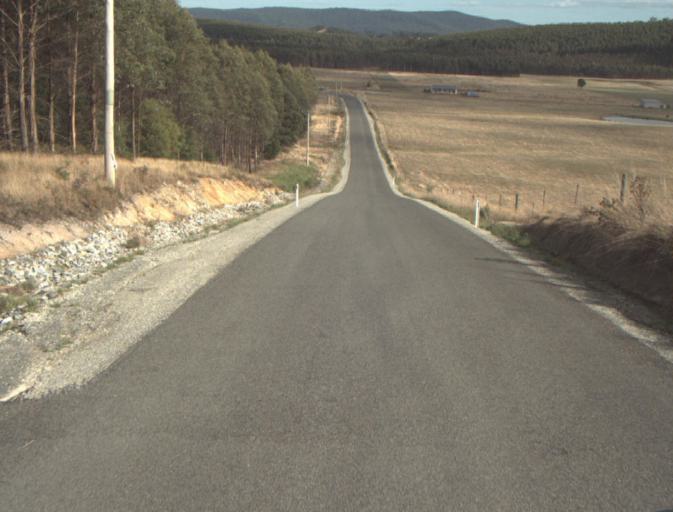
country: AU
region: Tasmania
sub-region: Launceston
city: Mayfield
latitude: -41.1939
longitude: 147.1818
